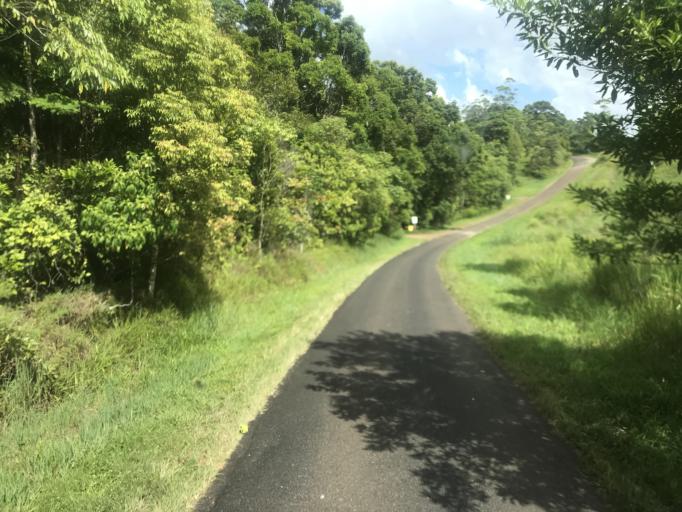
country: AU
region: Queensland
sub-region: Tablelands
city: Ravenshoe
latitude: -17.5443
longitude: 145.6929
